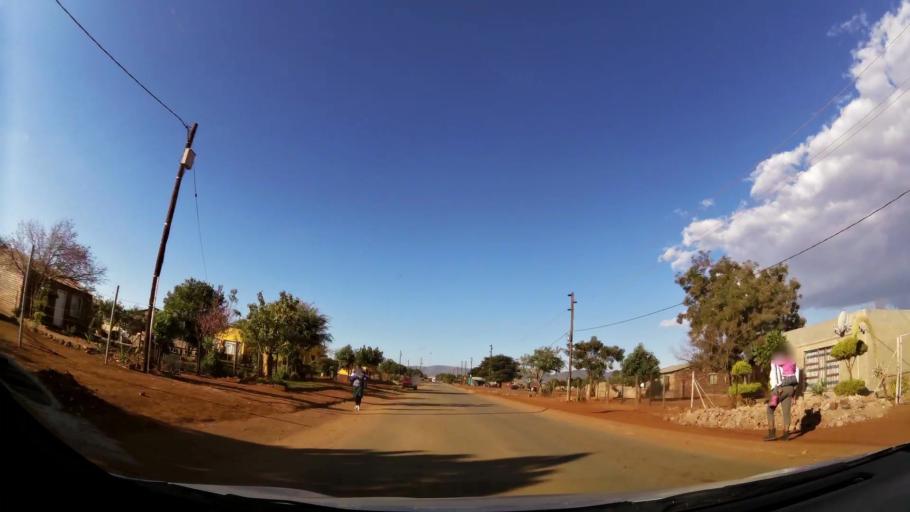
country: ZA
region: Limpopo
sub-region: Waterberg District Municipality
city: Mokopane
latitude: -24.1826
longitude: 28.9760
